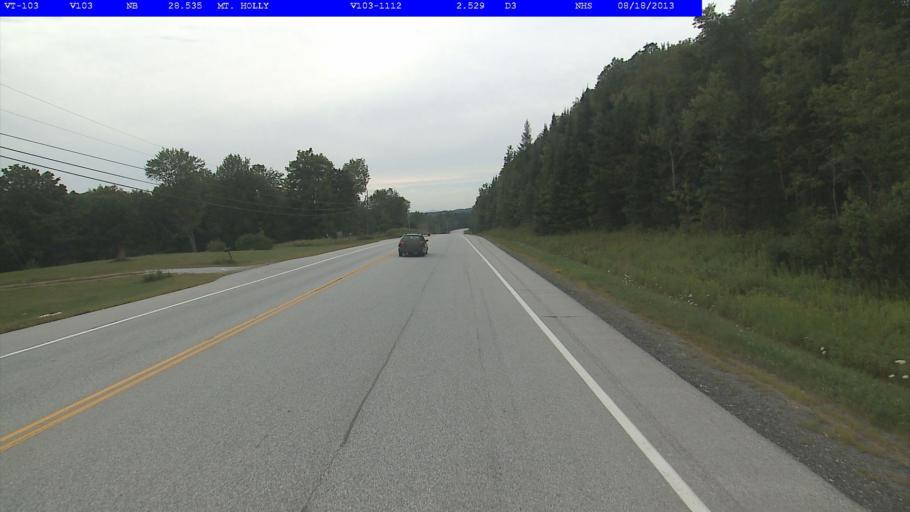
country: US
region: Vermont
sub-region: Rutland County
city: Rutland
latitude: 43.4481
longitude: -72.7777
